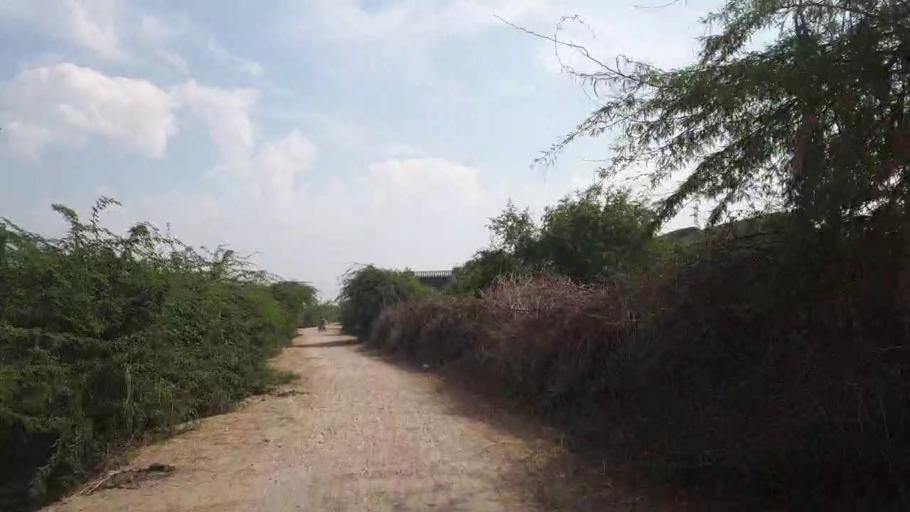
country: PK
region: Sindh
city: Tando Bago
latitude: 24.9359
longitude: 68.9998
